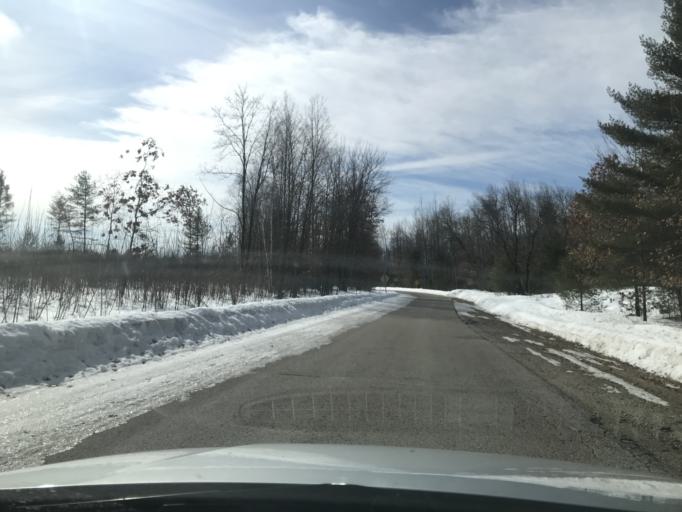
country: US
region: Wisconsin
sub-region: Menominee County
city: Legend Lake
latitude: 45.1120
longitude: -88.4432
